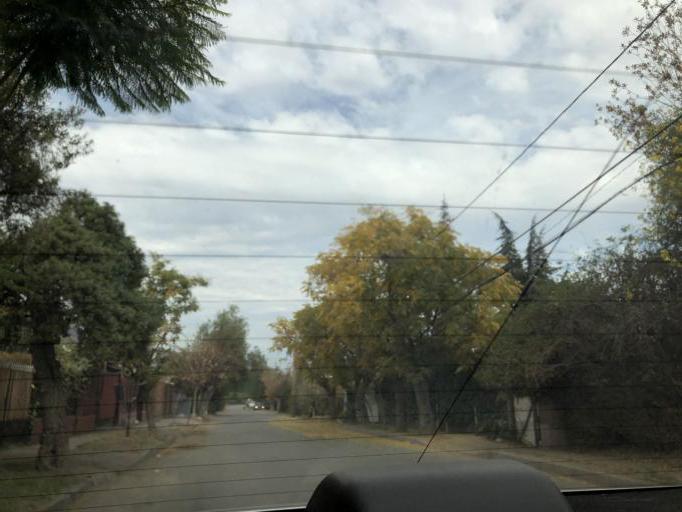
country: CL
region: Santiago Metropolitan
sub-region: Provincia de Cordillera
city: Puente Alto
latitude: -33.6115
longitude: -70.5332
